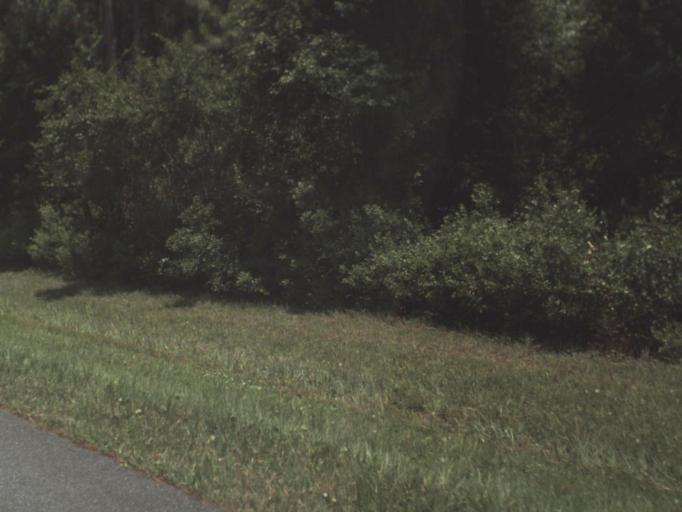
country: US
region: Florida
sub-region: Baker County
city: Macclenny
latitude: 30.1390
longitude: -82.1901
